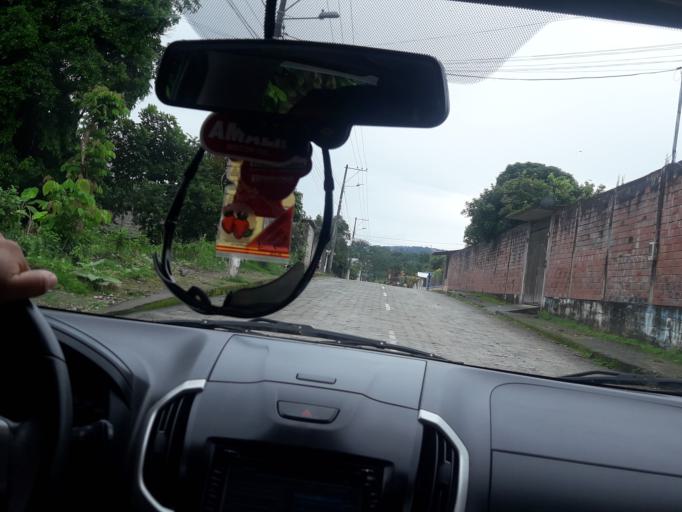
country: EC
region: Napo
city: Tena
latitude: -1.0422
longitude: -77.7925
